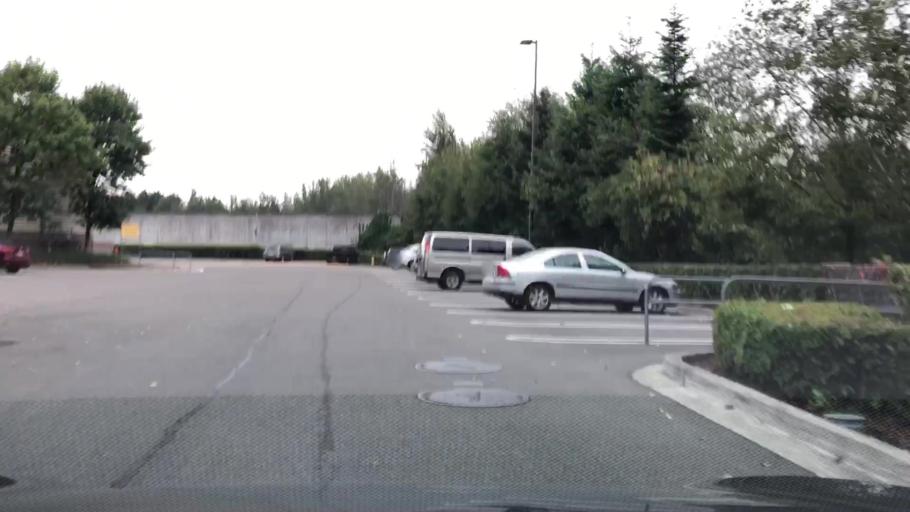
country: US
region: Washington
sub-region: King County
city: Woodinville
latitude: 47.7800
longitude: -122.1491
